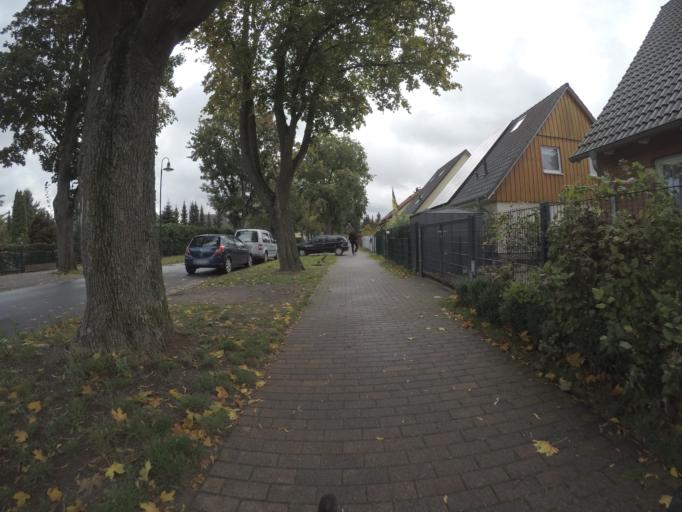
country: DE
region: Berlin
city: Lubars
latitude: 52.6312
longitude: 13.3684
